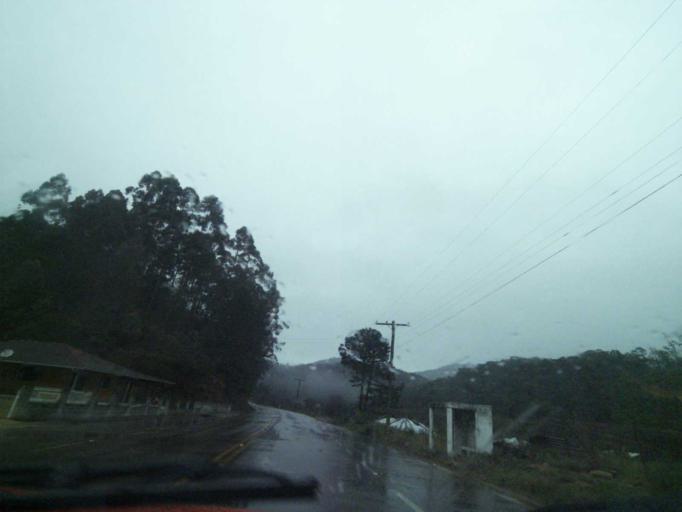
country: BR
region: Santa Catarina
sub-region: Anitapolis
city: Anitapolis
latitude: -27.8438
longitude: -49.0521
